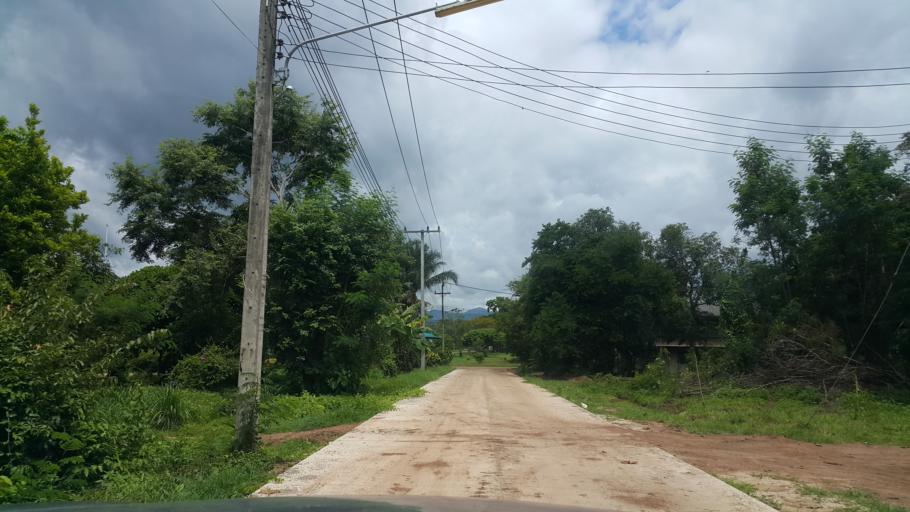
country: TH
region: Chiang Mai
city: Mae Taeng
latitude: 19.1696
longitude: 98.9519
